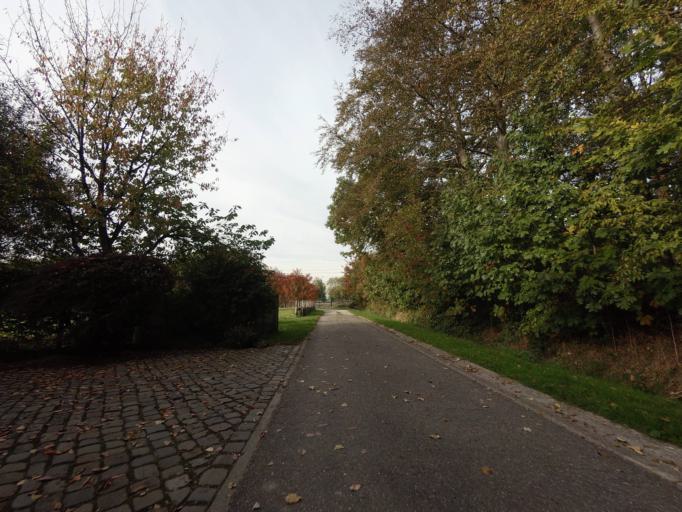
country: BE
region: Flanders
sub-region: Provincie Vlaams-Brabant
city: Kortenberg
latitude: 50.8965
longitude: 4.5918
